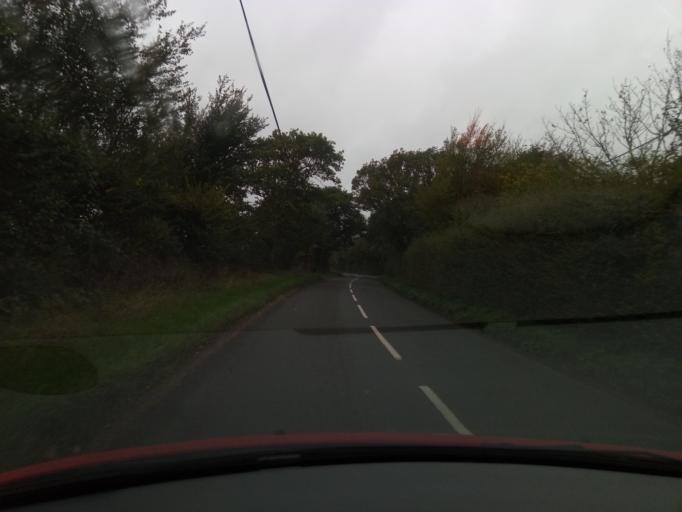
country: GB
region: England
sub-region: Essex
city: West Mersea
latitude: 51.7902
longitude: 0.9648
